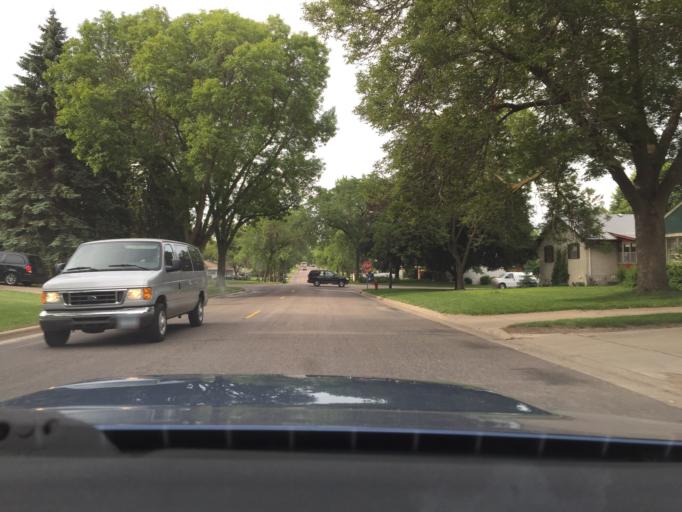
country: US
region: Minnesota
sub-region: Dakota County
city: West Saint Paul
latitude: 44.9059
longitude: -93.1019
